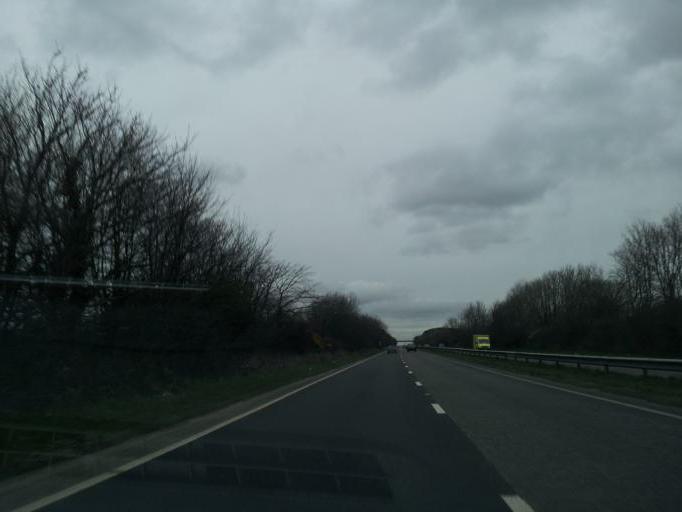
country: GB
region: England
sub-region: Cornwall
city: Redruth
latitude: 50.2493
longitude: -5.2224
